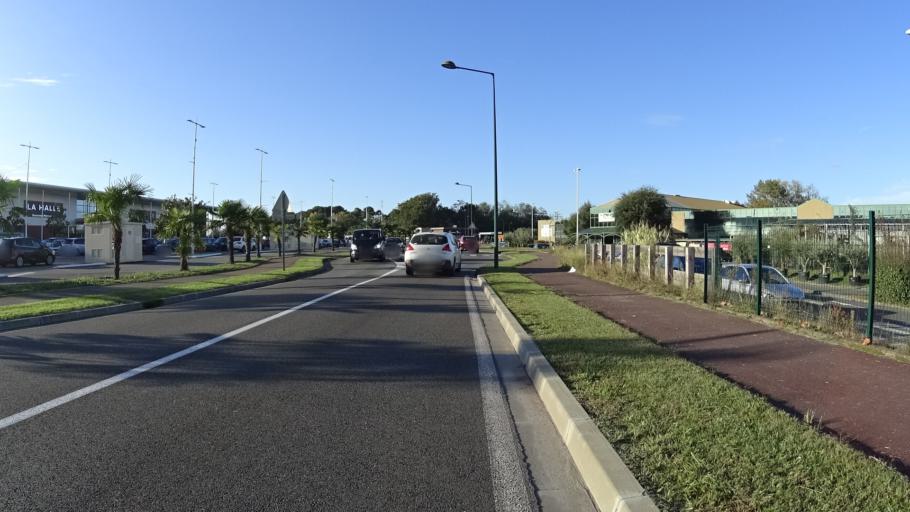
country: FR
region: Aquitaine
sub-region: Departement des Landes
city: Saint-Paul-les-Dax
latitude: 43.7303
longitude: -1.0384
